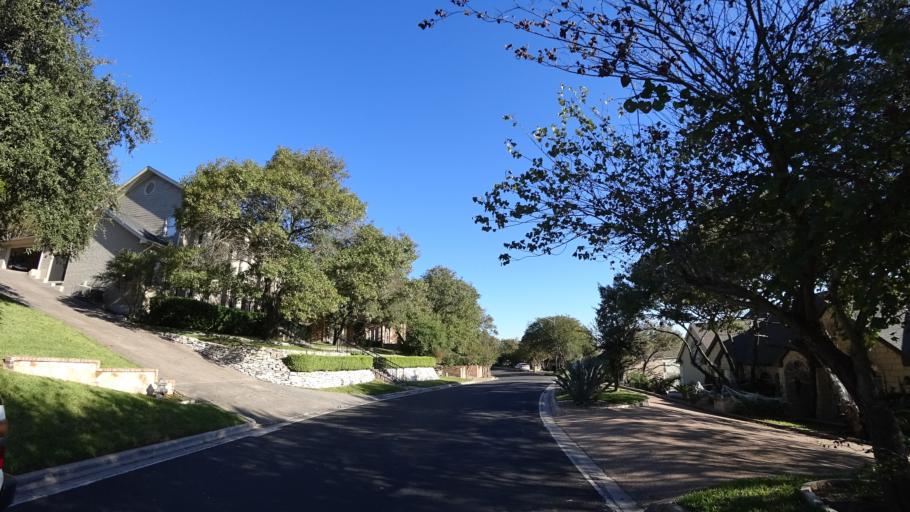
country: US
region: Texas
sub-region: Travis County
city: West Lake Hills
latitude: 30.3299
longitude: -97.8026
